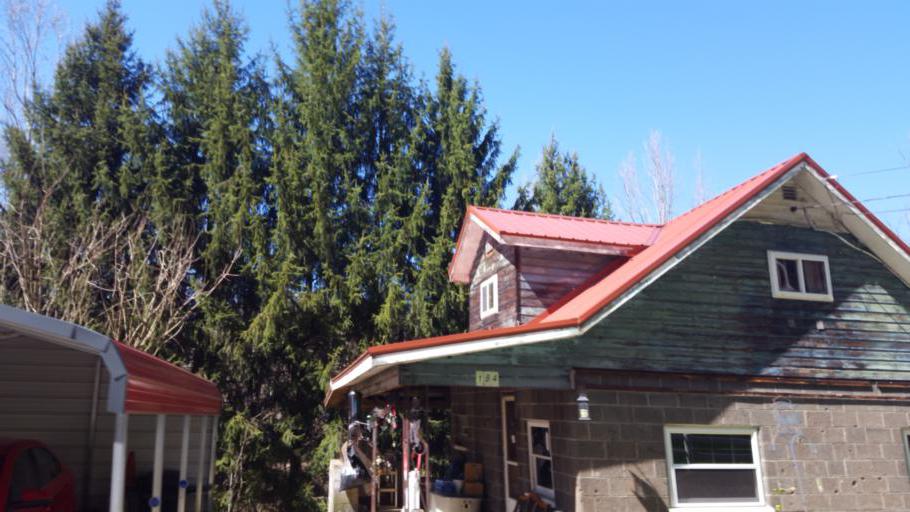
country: US
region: Ohio
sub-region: Jefferson County
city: Tiltonsville
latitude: 40.1834
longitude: -80.6965
